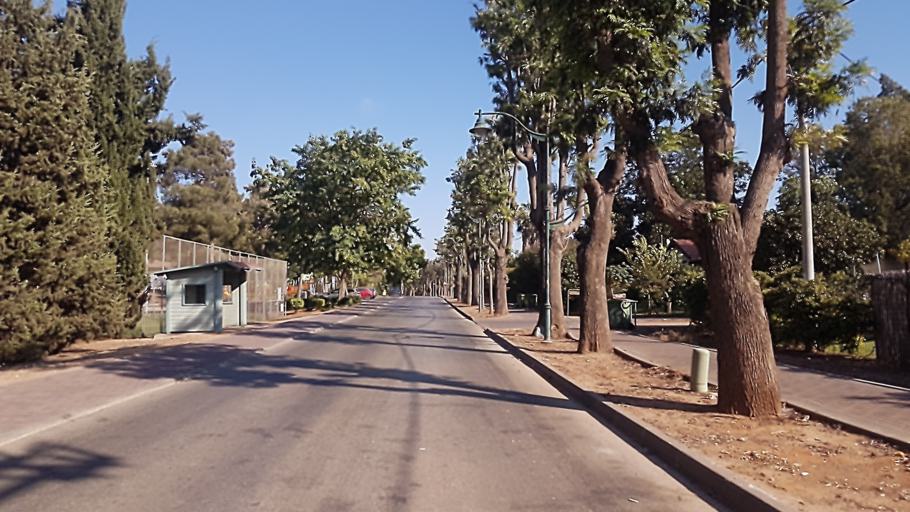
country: IL
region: Central District
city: Kfar Saba
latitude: 32.2105
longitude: 34.8985
